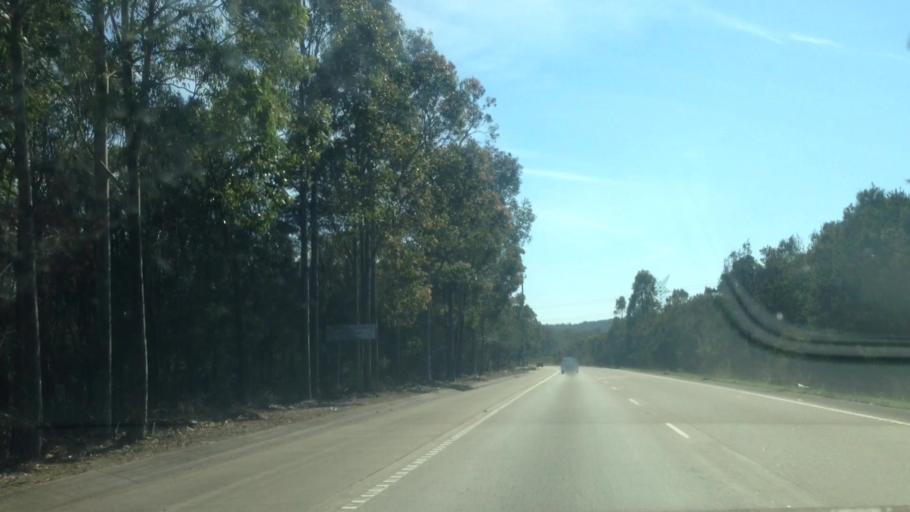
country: AU
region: New South Wales
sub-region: Lake Macquarie Shire
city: Fennell Bay
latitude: -32.9580
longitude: 151.5421
